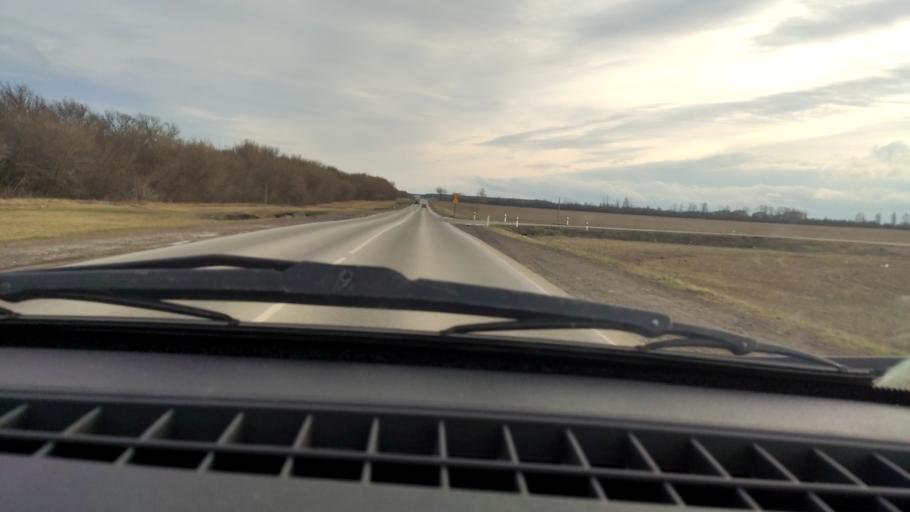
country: RU
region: Bashkortostan
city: Davlekanovo
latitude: 54.2753
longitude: 55.1036
